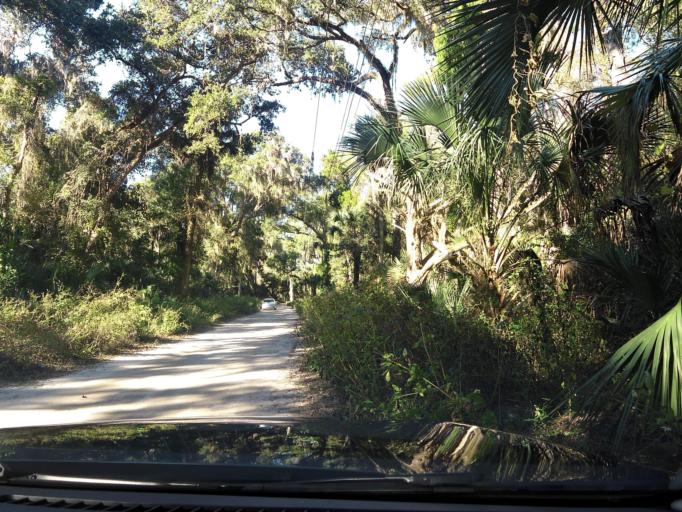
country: US
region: Florida
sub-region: Duval County
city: Atlantic Beach
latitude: 30.4159
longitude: -81.4326
